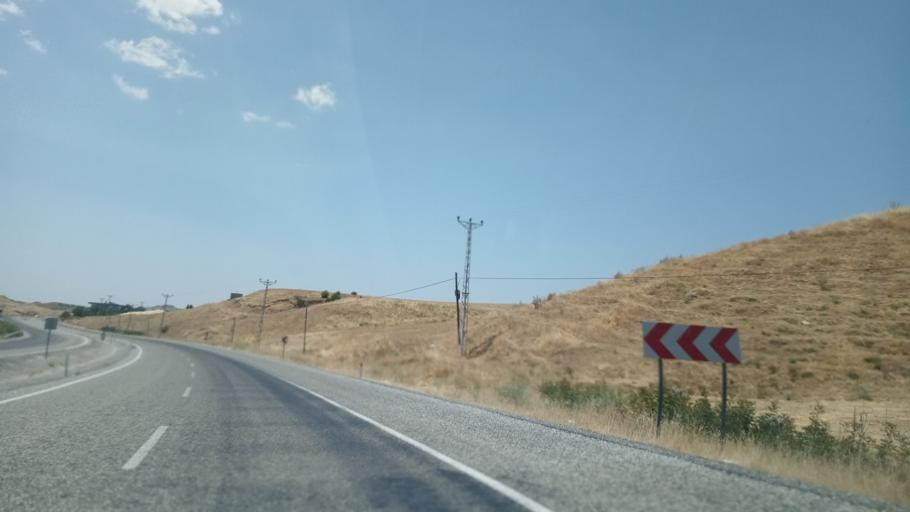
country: TR
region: Batman
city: Bekirhan
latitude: 38.1550
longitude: 41.3220
